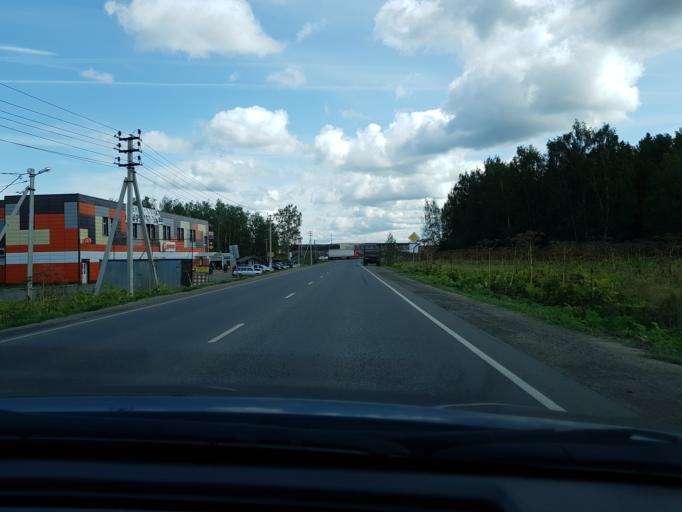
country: RU
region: Moskovskaya
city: Istra
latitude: 55.9717
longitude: 36.9510
